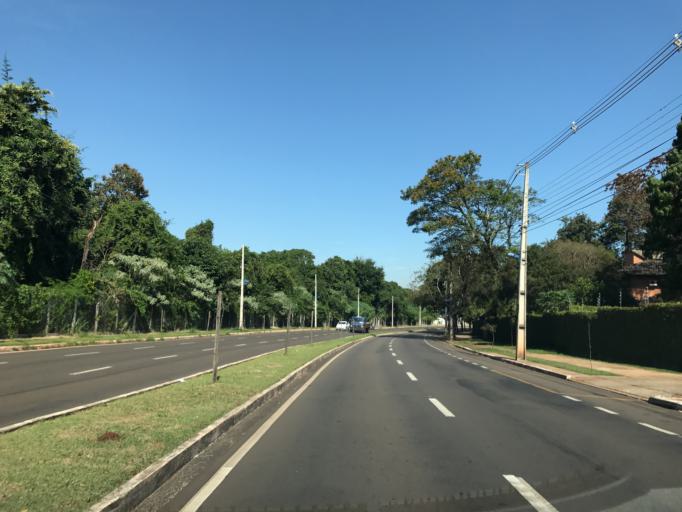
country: BR
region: Parana
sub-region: Maringa
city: Maringa
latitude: -23.4352
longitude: -51.9443
